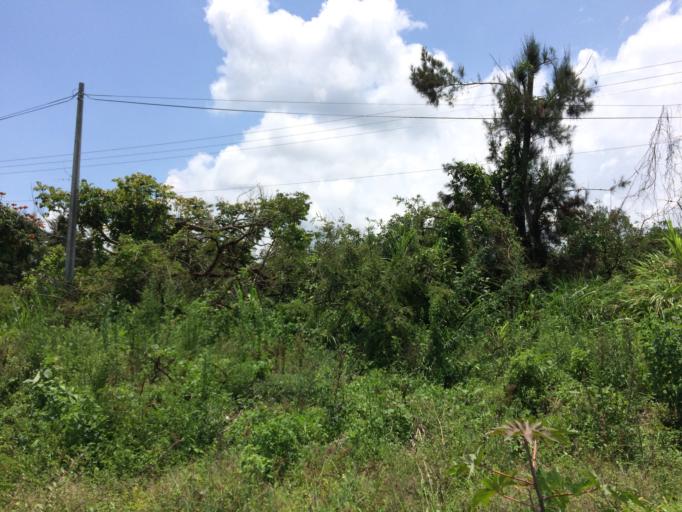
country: MX
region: Michoacan
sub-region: Periban
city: San Francisco Periban
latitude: 19.5452
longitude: -102.4070
